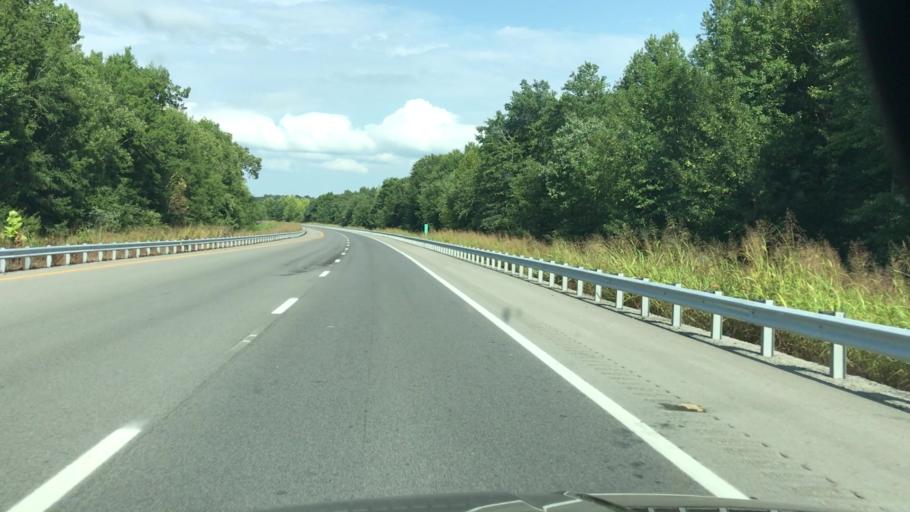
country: US
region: Kentucky
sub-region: Hopkins County
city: Nortonville
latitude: 37.2106
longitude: -87.4123
